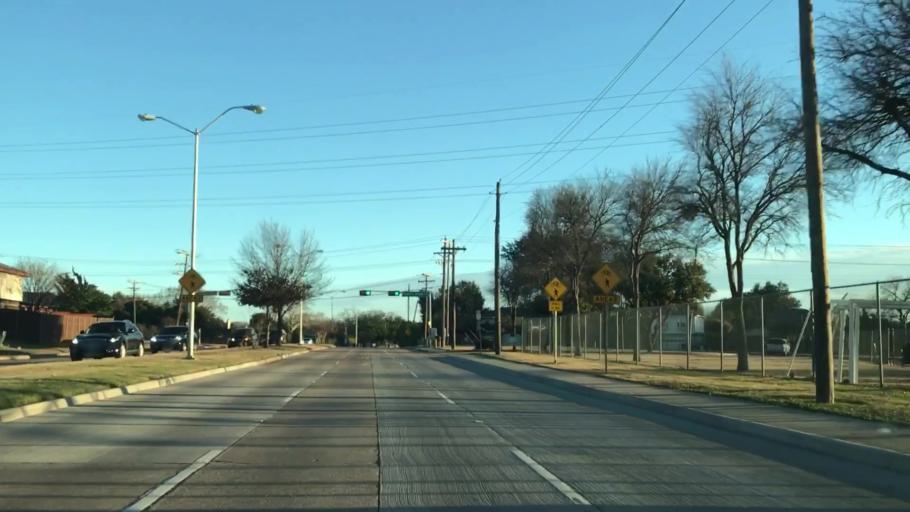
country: US
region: Texas
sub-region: Dallas County
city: Addison
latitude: 32.9772
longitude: -96.7855
